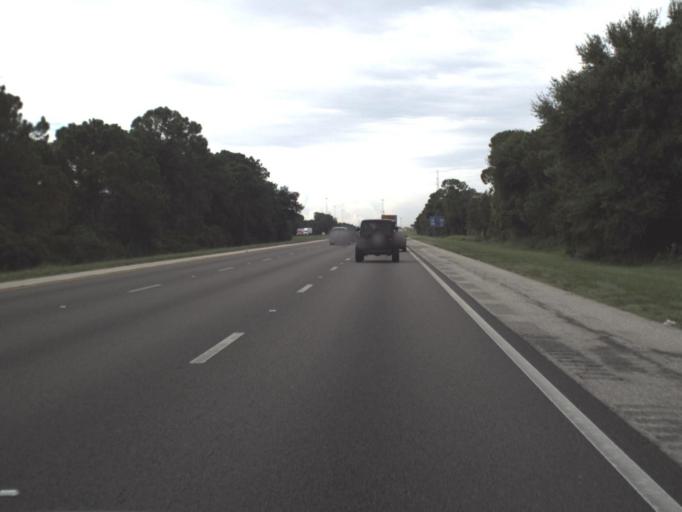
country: US
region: Florida
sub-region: Sarasota County
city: The Meadows
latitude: 27.3525
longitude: -82.4468
